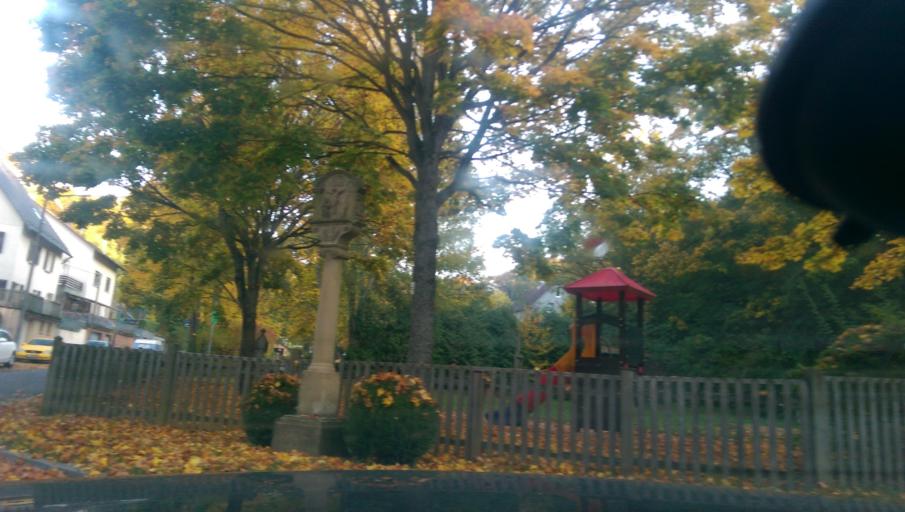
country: DE
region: Bavaria
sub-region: Regierungsbezirk Unterfranken
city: Schonungen
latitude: 50.0591
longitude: 10.2900
